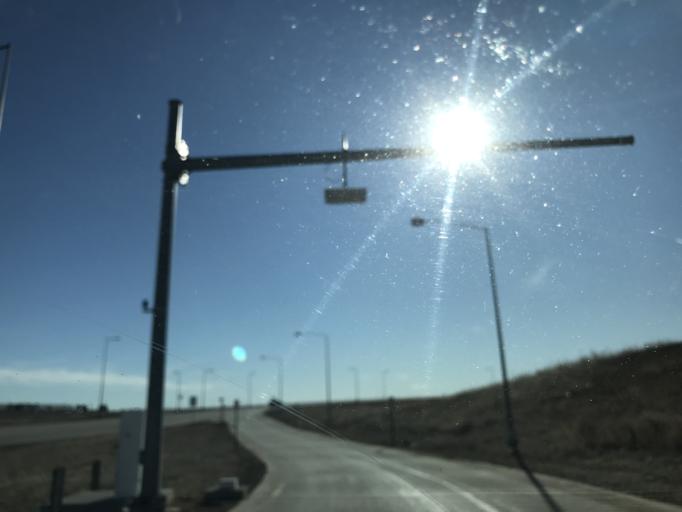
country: US
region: Colorado
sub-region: Weld County
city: Lochbuie
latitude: 39.8457
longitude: -104.6717
